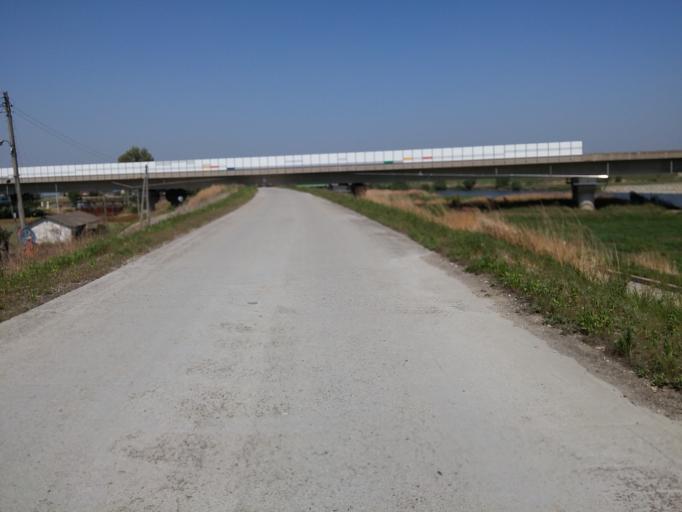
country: KR
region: Chungcheongnam-do
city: Nonsan
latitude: 36.1839
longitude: 127.0498
